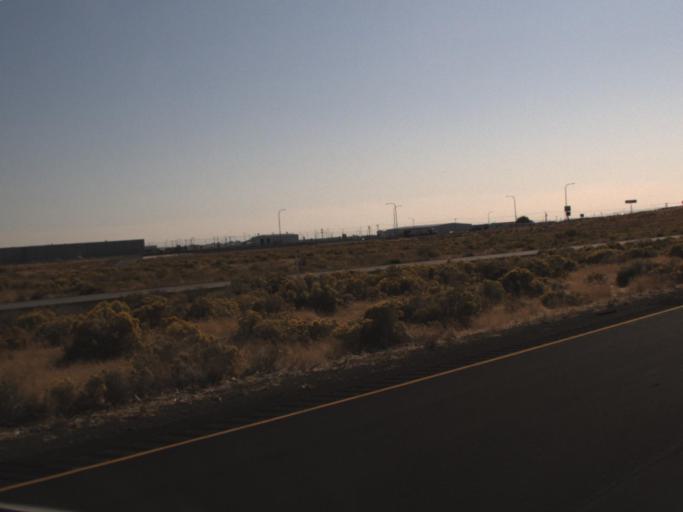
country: US
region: Washington
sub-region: Franklin County
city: Pasco
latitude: 46.2676
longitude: -119.0879
